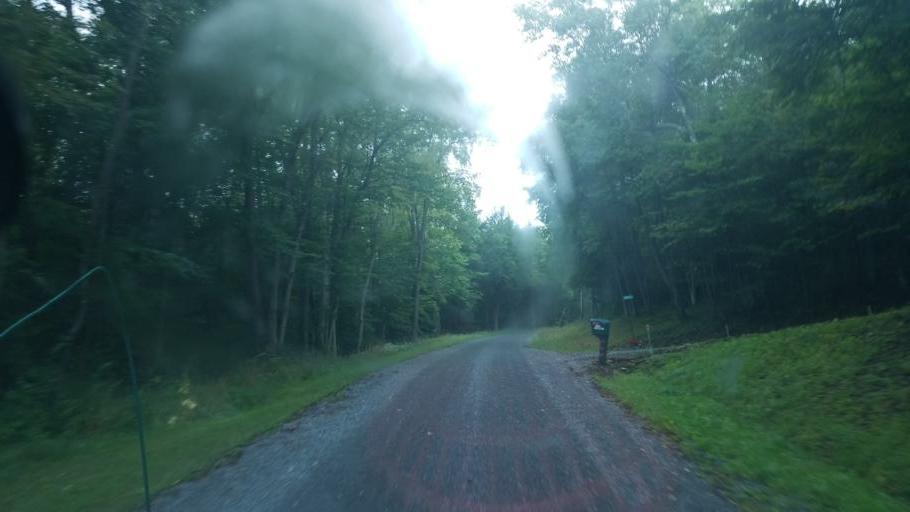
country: US
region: Pennsylvania
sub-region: Potter County
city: Galeton
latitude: 41.8389
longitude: -77.7956
